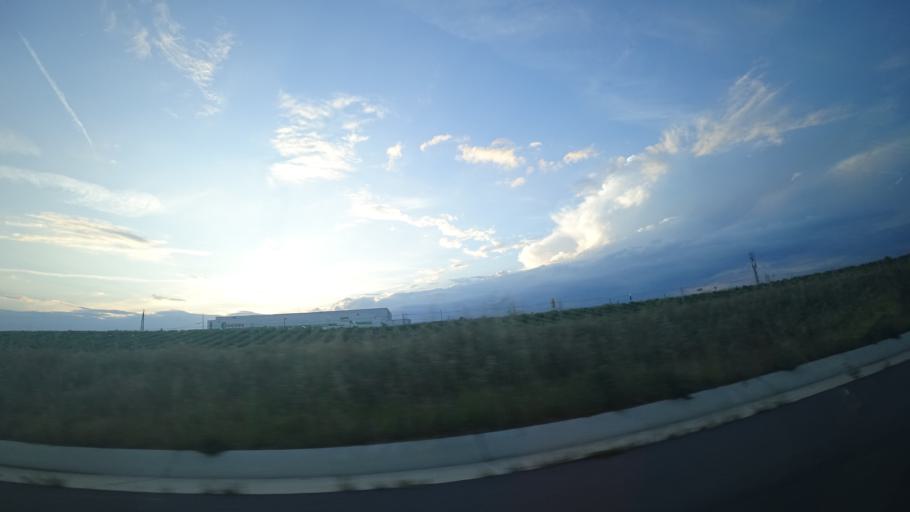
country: FR
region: Languedoc-Roussillon
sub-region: Departement de l'Herault
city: Servian
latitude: 43.3874
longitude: 3.3154
